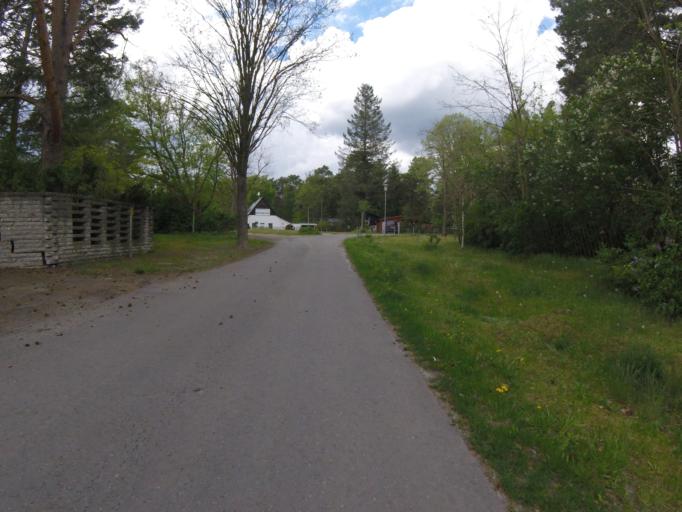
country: DE
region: Brandenburg
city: Schwerin
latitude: 52.1581
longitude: 13.6295
